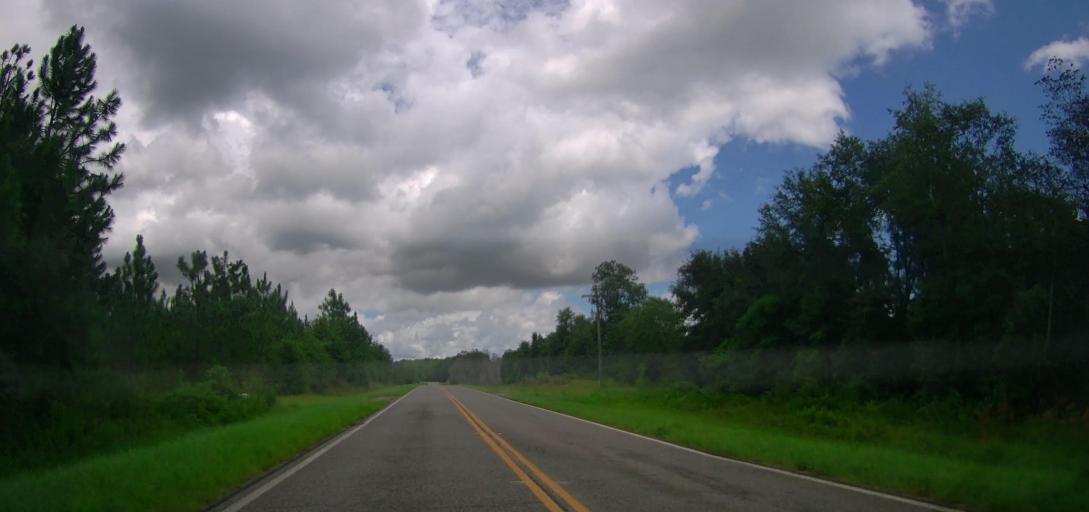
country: US
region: Georgia
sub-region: Wilcox County
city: Rochelle
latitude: 31.9329
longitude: -83.5494
